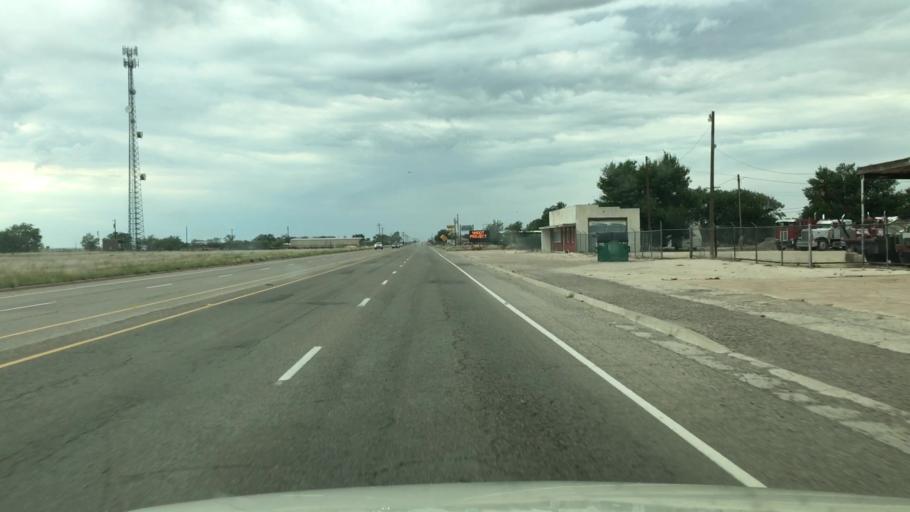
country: US
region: New Mexico
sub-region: Lea County
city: Lovington
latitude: 33.2570
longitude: -103.3302
